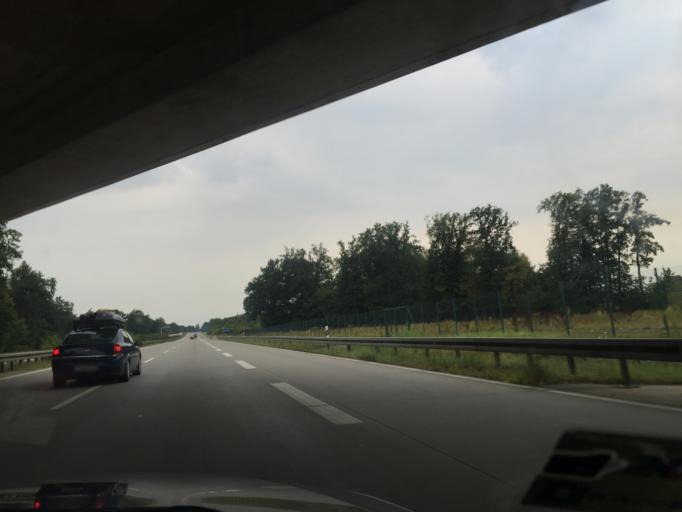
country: DE
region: Brandenburg
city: Bernau bei Berlin
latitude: 52.6921
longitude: 13.5575
